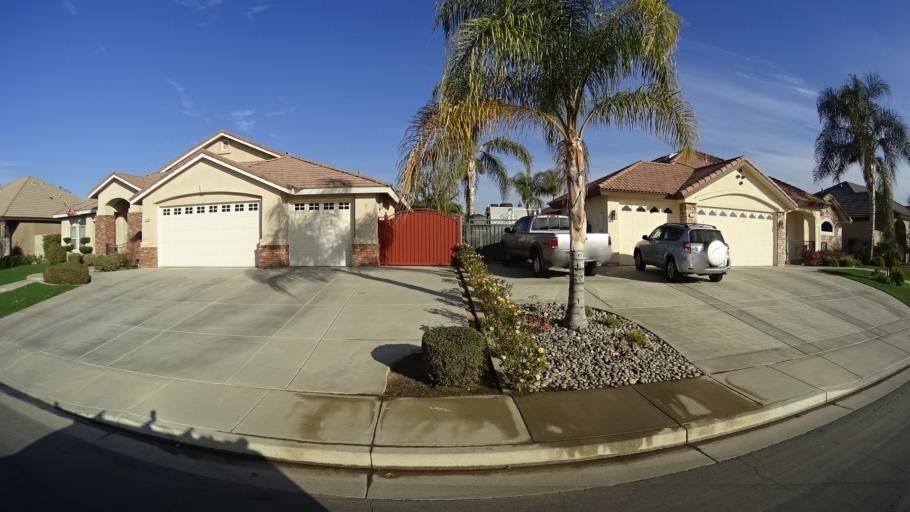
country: US
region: California
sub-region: Kern County
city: Rosedale
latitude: 35.4102
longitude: -119.1334
